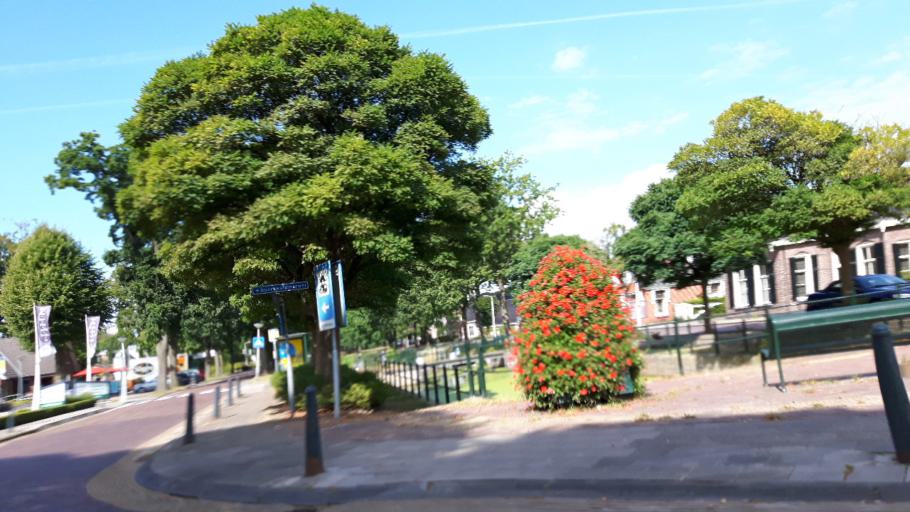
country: NL
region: Friesland
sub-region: Gemeente Smallingerland
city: Drachtstercompagnie
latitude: 53.0806
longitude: 6.2565
